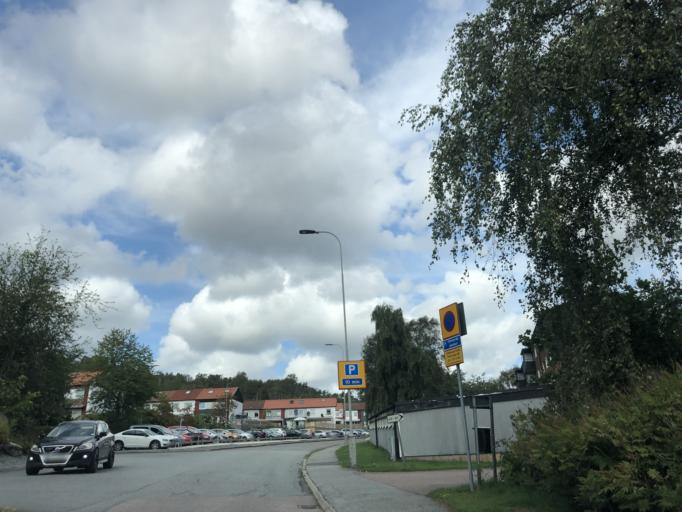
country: SE
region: Vaestra Goetaland
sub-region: Goteborg
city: Majorna
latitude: 57.7105
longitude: 11.8856
